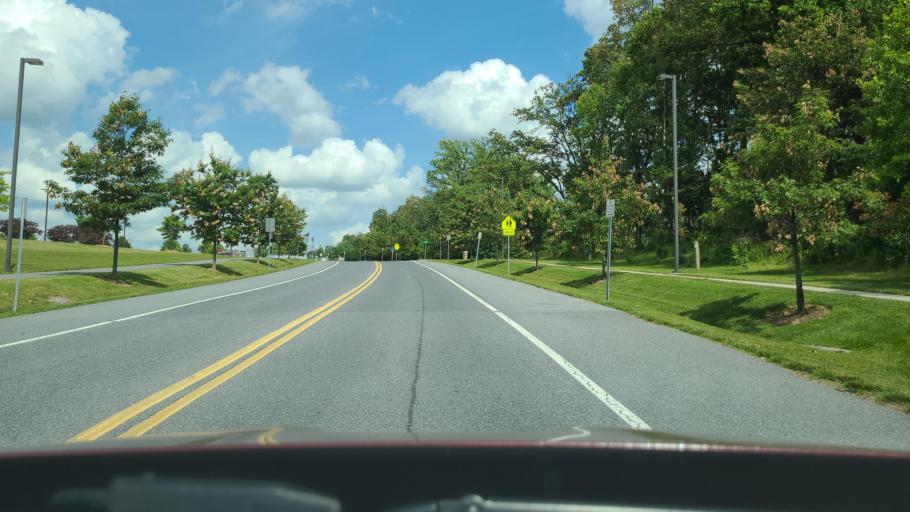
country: US
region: Maryland
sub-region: Montgomery County
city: Clarksburg
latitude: 39.2307
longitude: -77.2400
